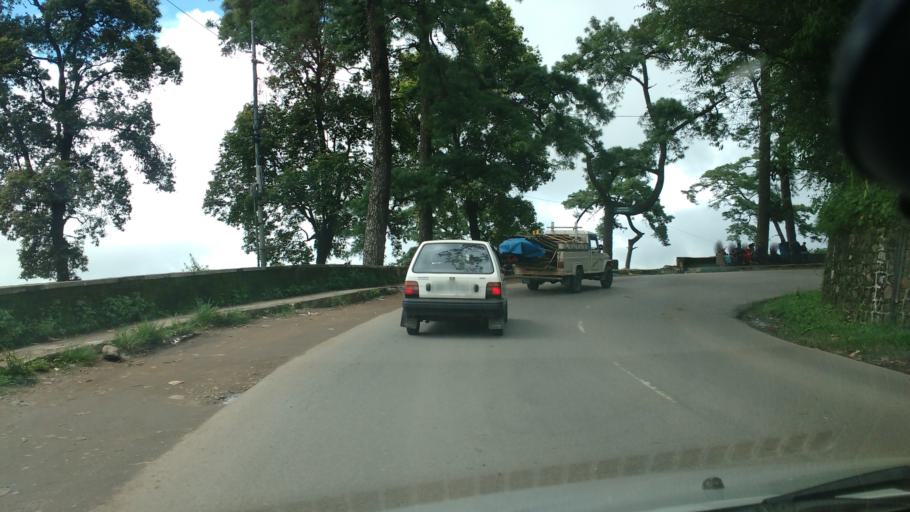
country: IN
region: Meghalaya
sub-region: East Khasi Hills
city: Shillong
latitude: 25.5662
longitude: 91.8552
